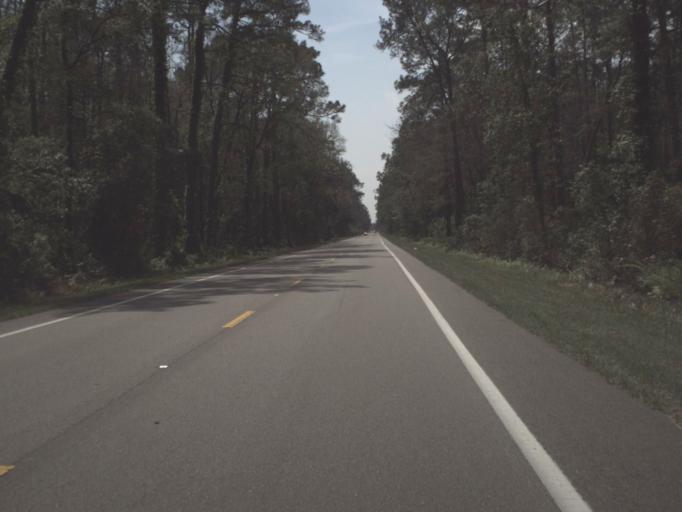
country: US
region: Florida
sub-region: Lake County
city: Umatilla
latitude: 29.0295
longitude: -81.6402
